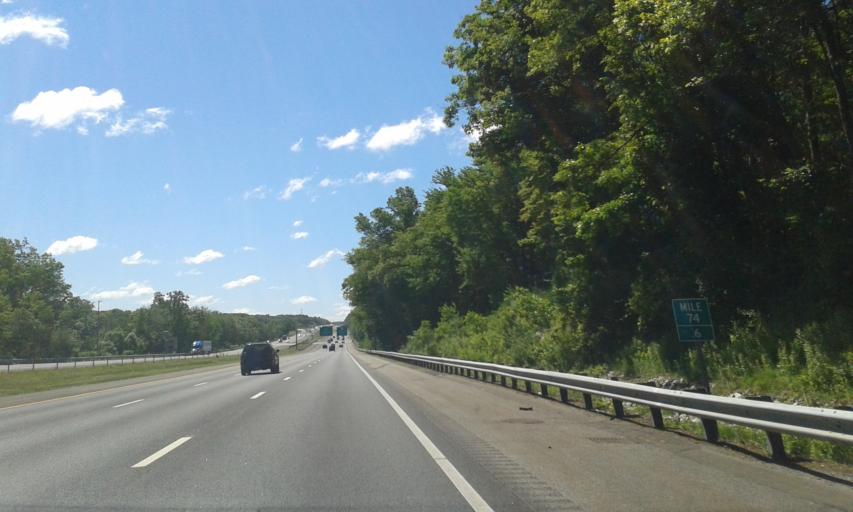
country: US
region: Massachusetts
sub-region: Middlesex County
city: Pinehurst
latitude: 42.5127
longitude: -71.2543
